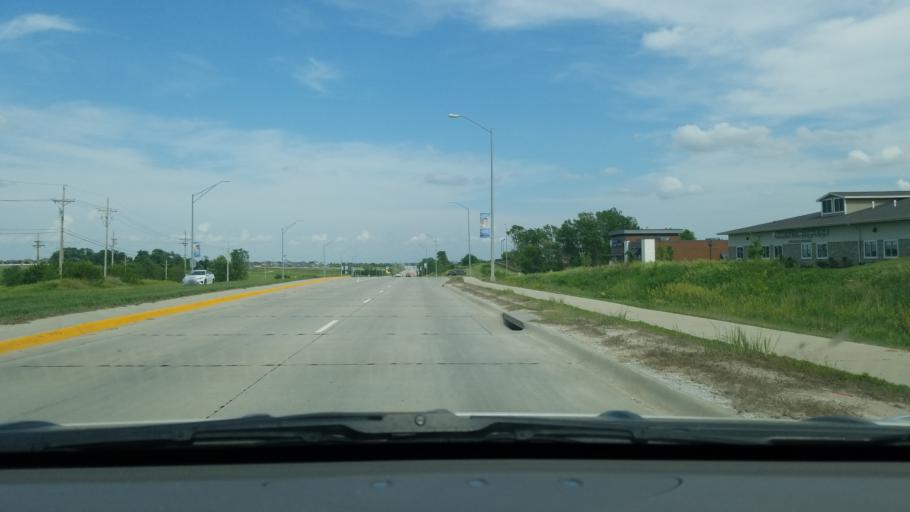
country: US
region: Nebraska
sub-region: Sarpy County
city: Gretna
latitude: 41.1469
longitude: -96.2305
